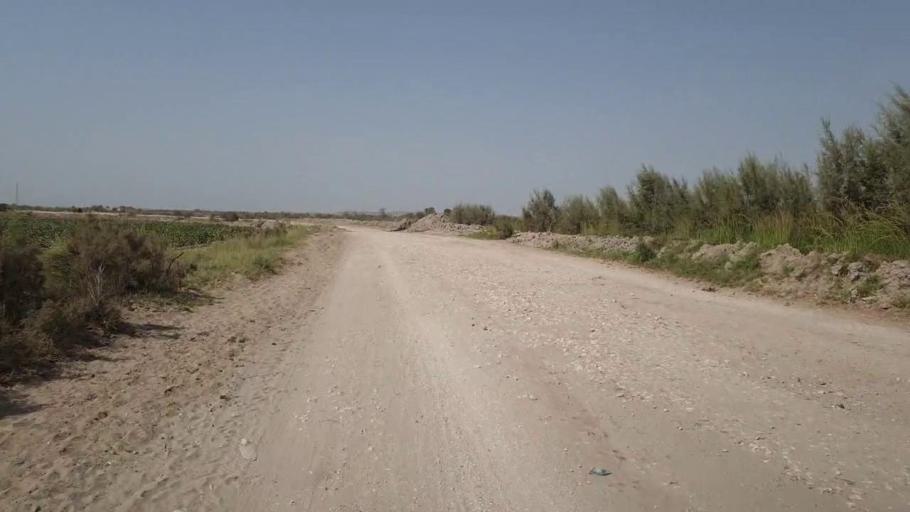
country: PK
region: Sindh
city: Jam Sahib
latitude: 26.4123
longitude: 68.9101
